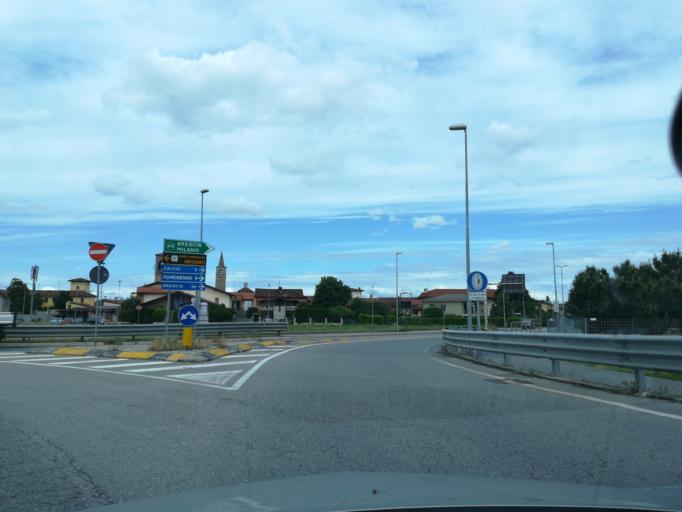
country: IT
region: Lombardy
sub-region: Provincia di Bergamo
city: Antegnate
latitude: 45.4823
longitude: 9.7911
